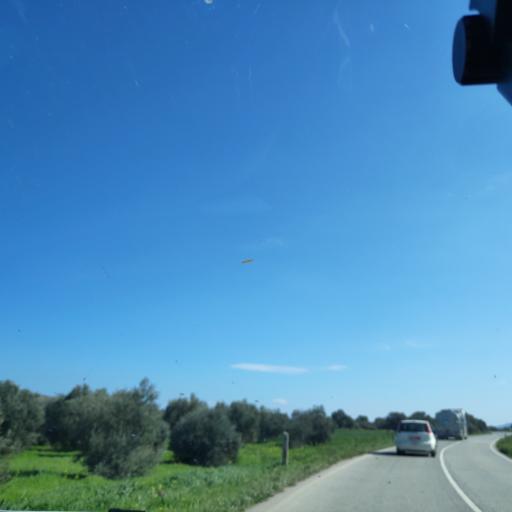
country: CY
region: Lefkosia
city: Tseri
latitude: 35.0170
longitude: 33.3350
